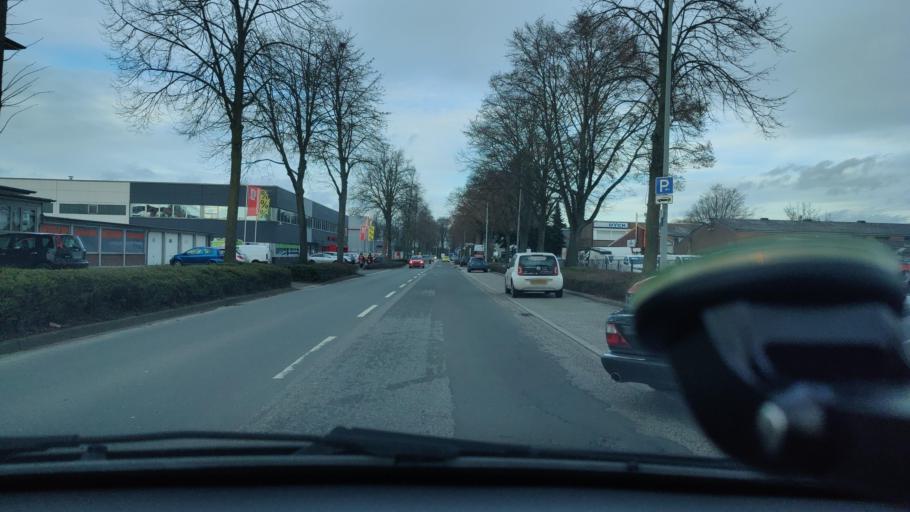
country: DE
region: North Rhine-Westphalia
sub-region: Regierungsbezirk Dusseldorf
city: Wesel
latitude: 51.6649
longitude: 6.6669
